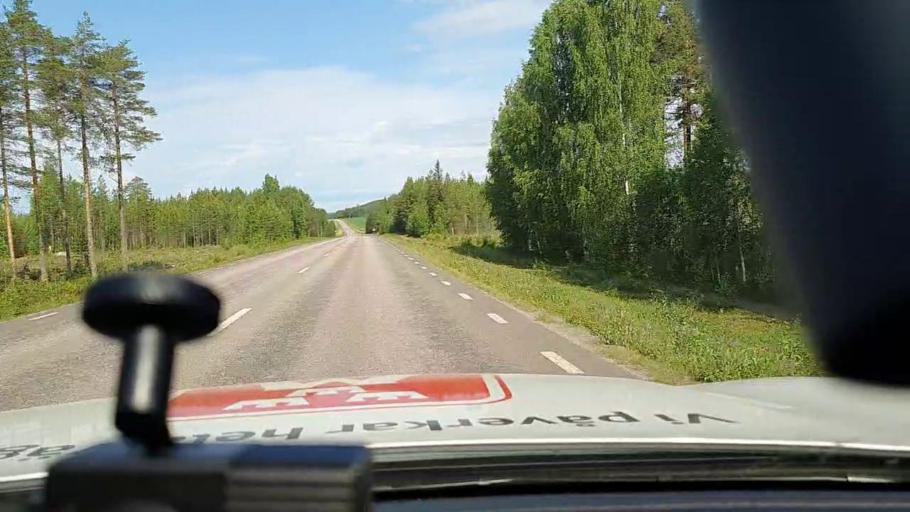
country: SE
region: Norrbotten
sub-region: Bodens Kommun
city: Boden
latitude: 65.9078
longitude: 21.3572
